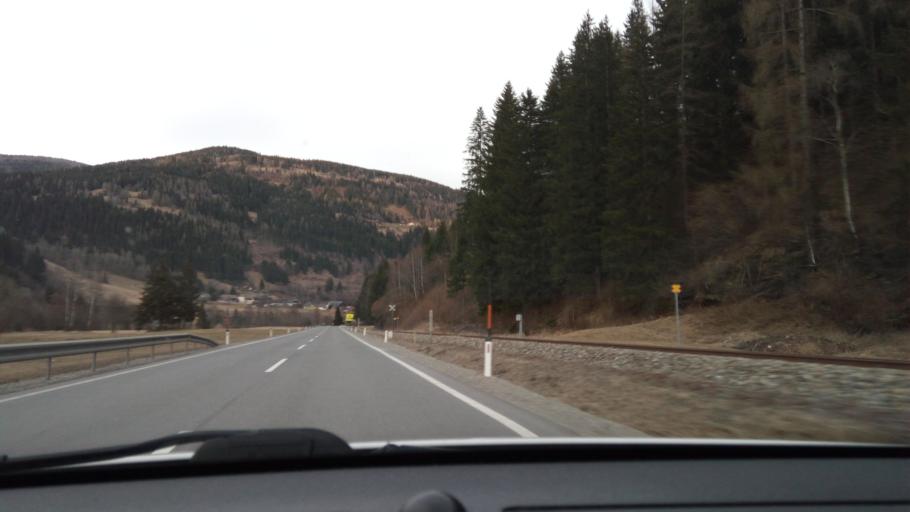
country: AT
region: Styria
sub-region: Politischer Bezirk Murau
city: Stadl an der Mur
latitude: 47.0809
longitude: 13.9317
